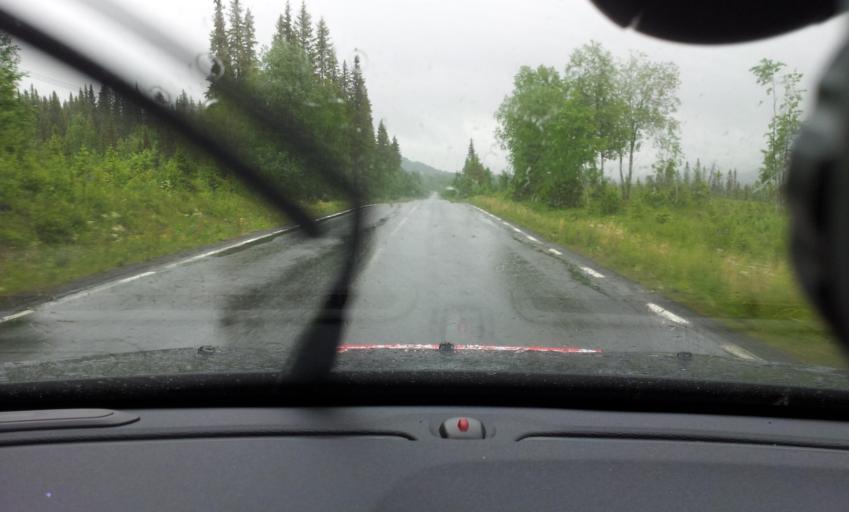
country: SE
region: Jaemtland
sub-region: Are Kommun
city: Are
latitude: 63.3153
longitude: 13.1231
